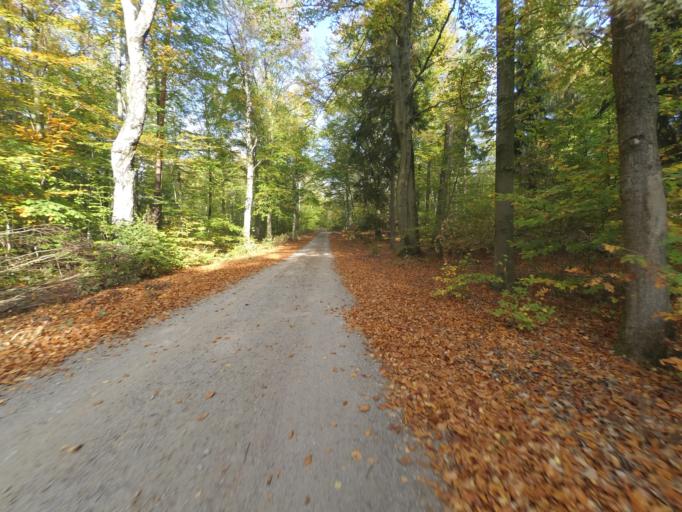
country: DE
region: Saxony
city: Albertstadt
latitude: 51.0981
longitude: 13.8045
